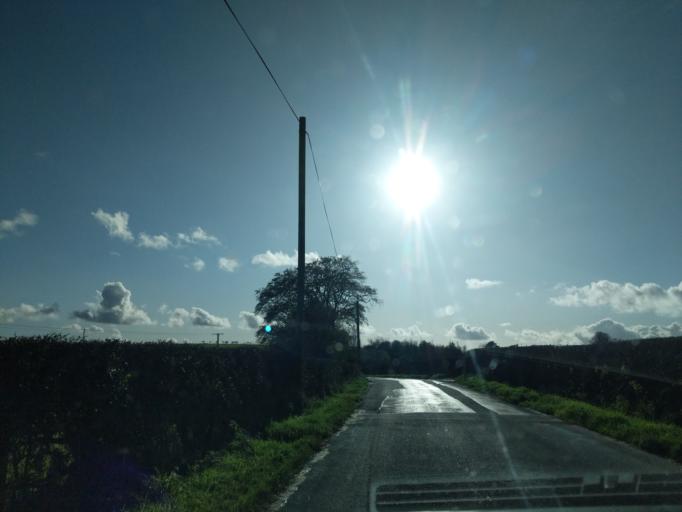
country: GB
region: Scotland
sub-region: Dumfries and Galloway
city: Dalbeattie
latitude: 55.0189
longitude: -3.7959
